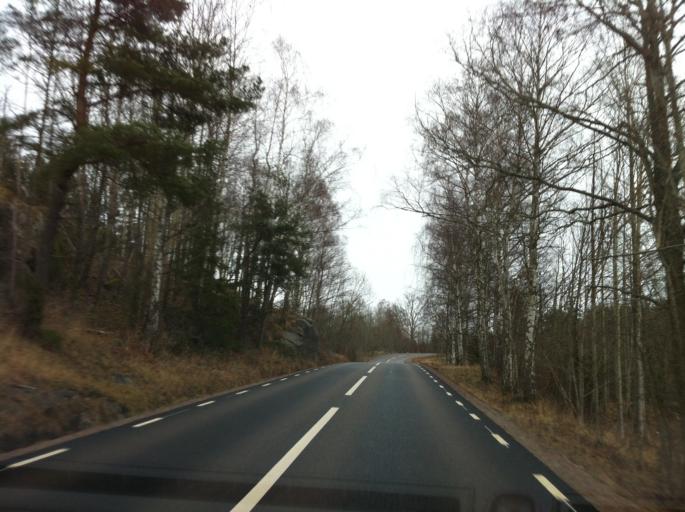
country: SE
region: Kalmar
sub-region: Vasterviks Kommun
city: Overum
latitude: 57.9052
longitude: 16.2270
